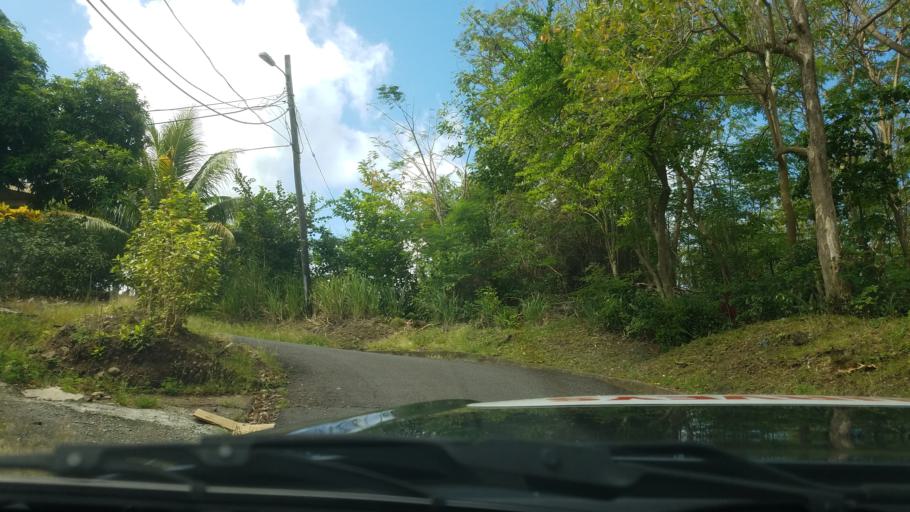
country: LC
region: Castries Quarter
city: Bisee
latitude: 14.0171
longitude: -60.9847
